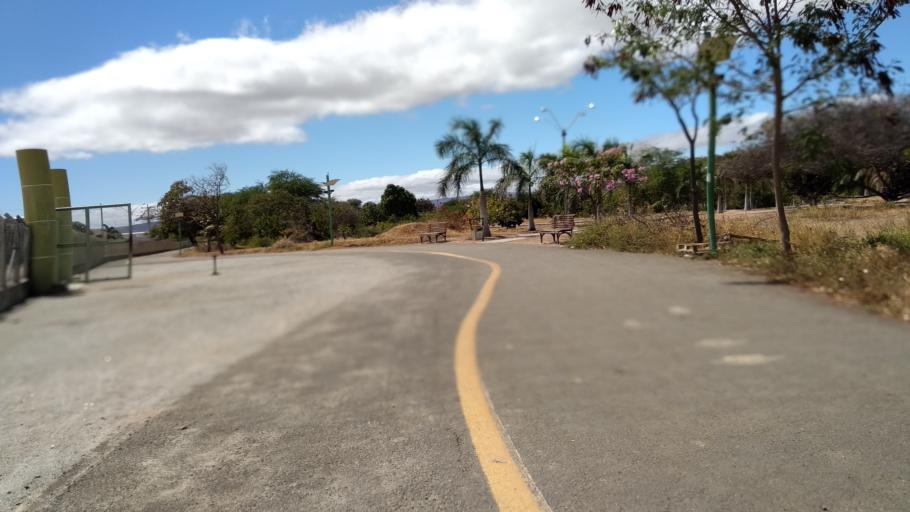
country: BR
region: Bahia
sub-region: Guanambi
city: Guanambi
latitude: -14.2250
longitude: -42.7656
